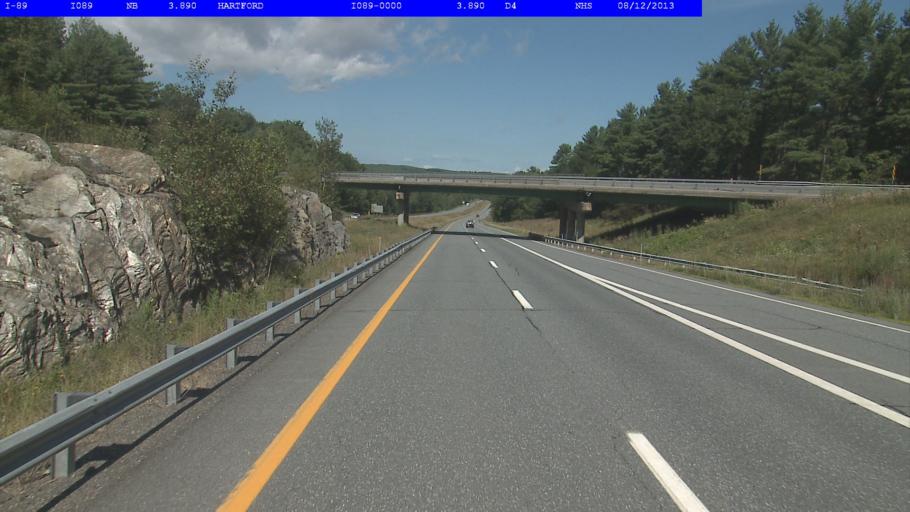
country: US
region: Vermont
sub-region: Windsor County
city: White River Junction
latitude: 43.6665
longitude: -72.3849
